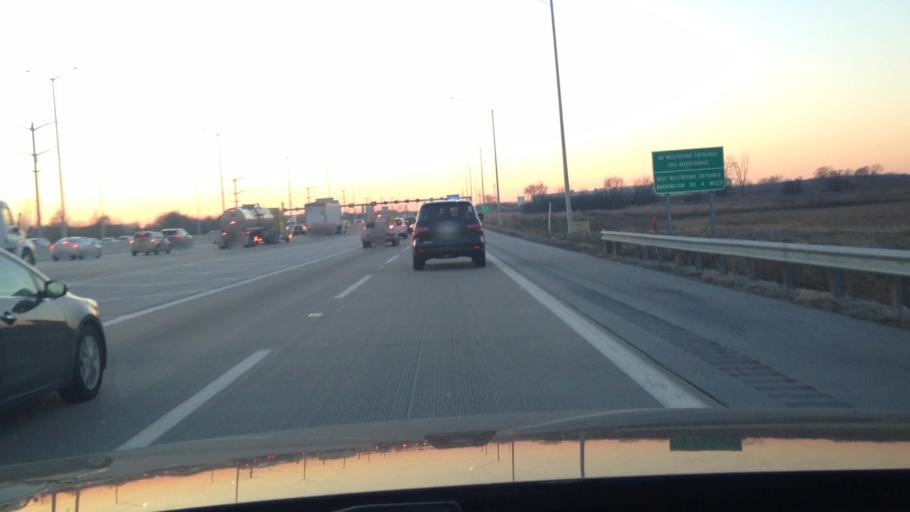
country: US
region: Illinois
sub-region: Cook County
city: Hoffman Estates
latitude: 42.0616
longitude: -88.0579
